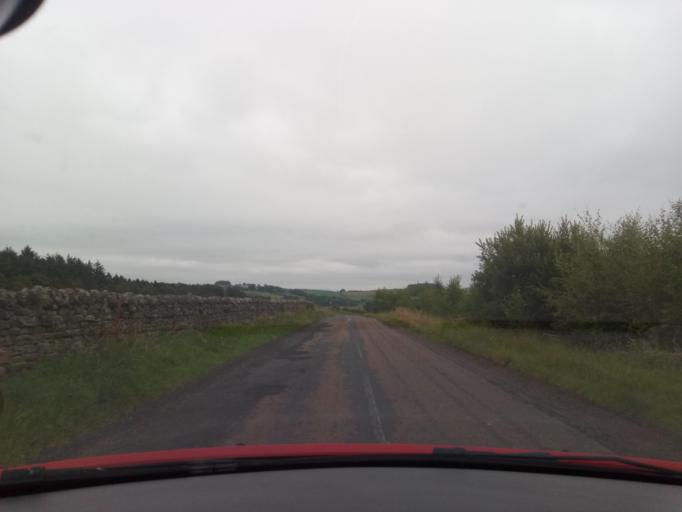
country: GB
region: England
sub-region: Northumberland
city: Otterburn
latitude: 55.3318
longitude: -2.0941
